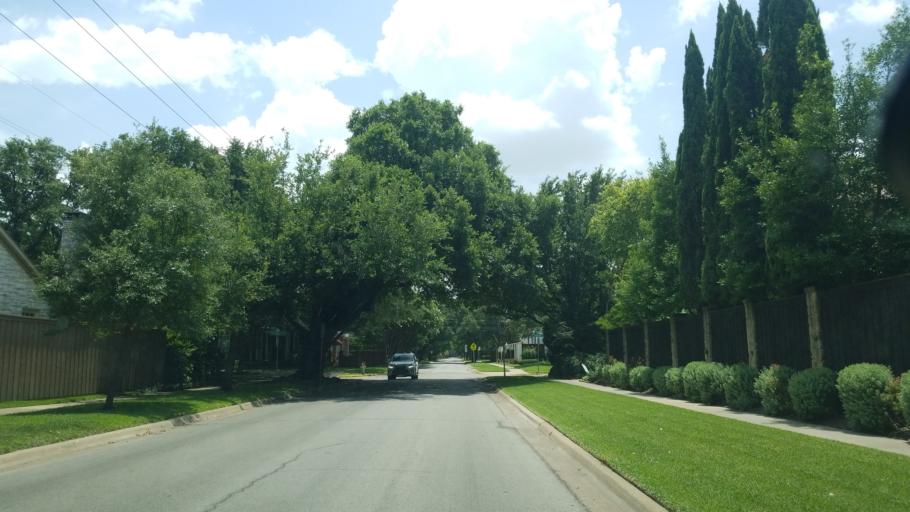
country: US
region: Texas
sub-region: Dallas County
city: University Park
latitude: 32.8627
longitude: -96.8019
